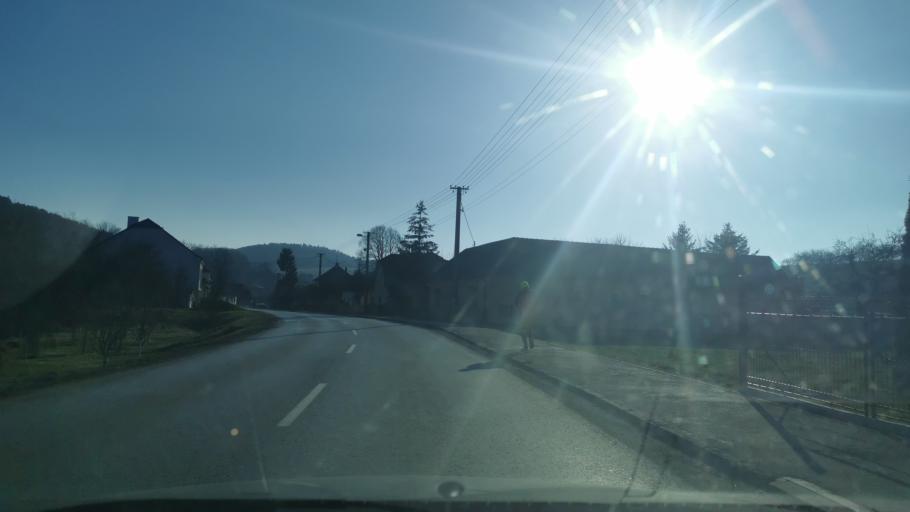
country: SK
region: Trenciansky
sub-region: Okres Myjava
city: Myjava
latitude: 48.7471
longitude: 17.5458
